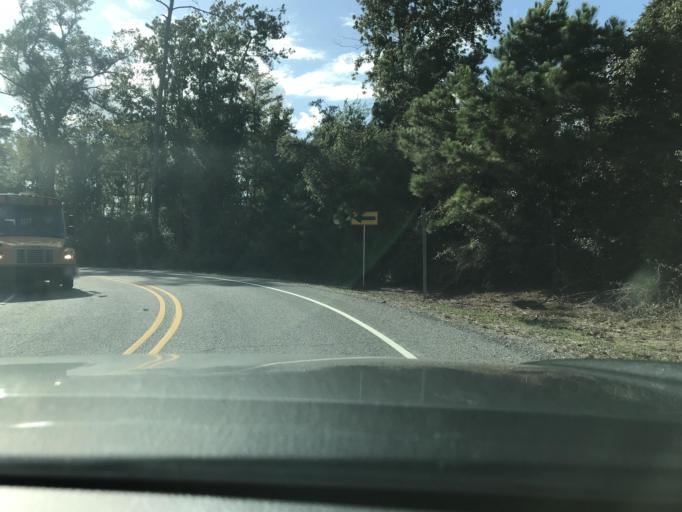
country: US
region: Louisiana
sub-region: Calcasieu Parish
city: Westlake
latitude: 30.3225
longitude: -93.2884
